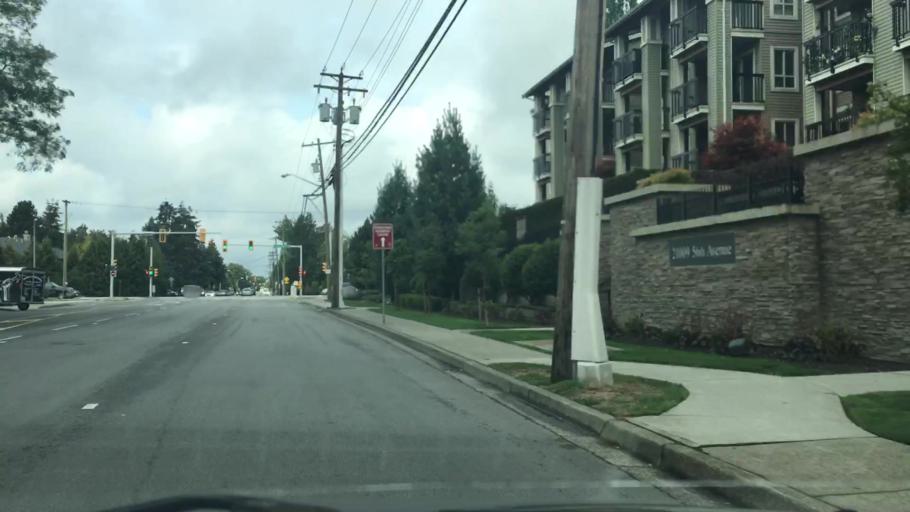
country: CA
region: British Columbia
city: Langley
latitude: 49.1047
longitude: -122.6415
